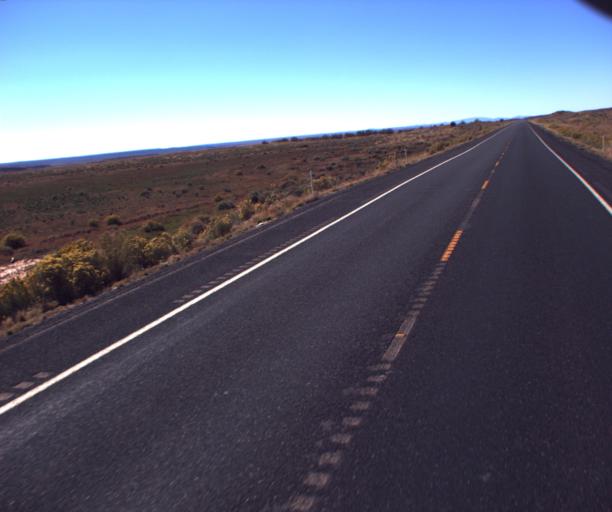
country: US
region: Arizona
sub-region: Coconino County
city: Fredonia
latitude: 36.9383
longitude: -112.5508
